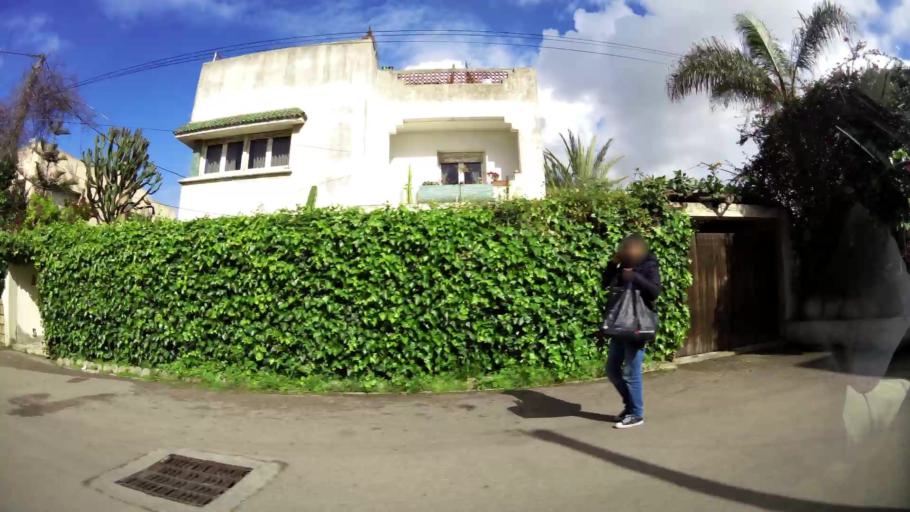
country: MA
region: Grand Casablanca
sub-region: Casablanca
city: Casablanca
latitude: 33.5478
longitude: -7.6249
